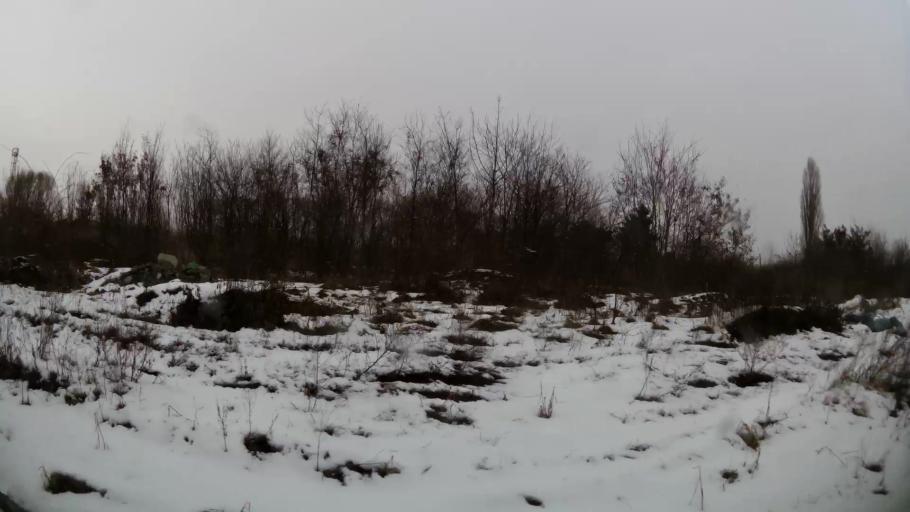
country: RO
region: Ilfov
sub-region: Comuna Mogosoaia
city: Mogosoaia
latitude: 44.5131
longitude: 26.0274
